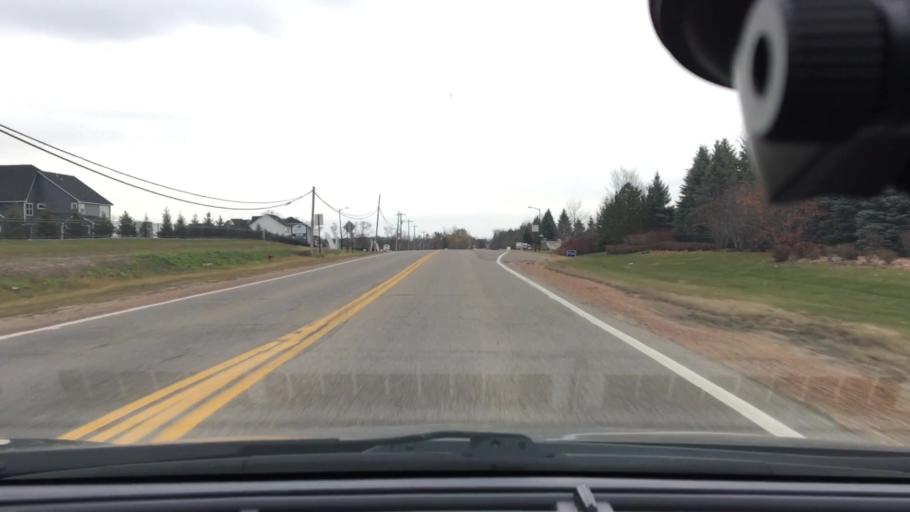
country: US
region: Minnesota
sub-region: Hennepin County
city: Corcoran
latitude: 45.0914
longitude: -93.5124
